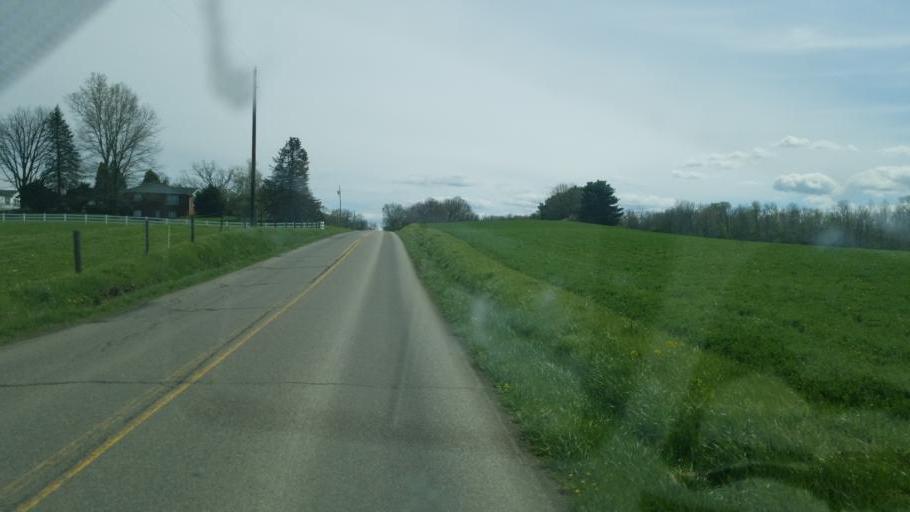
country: US
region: Ohio
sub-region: Holmes County
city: Millersburg
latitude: 40.6025
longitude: -81.8201
